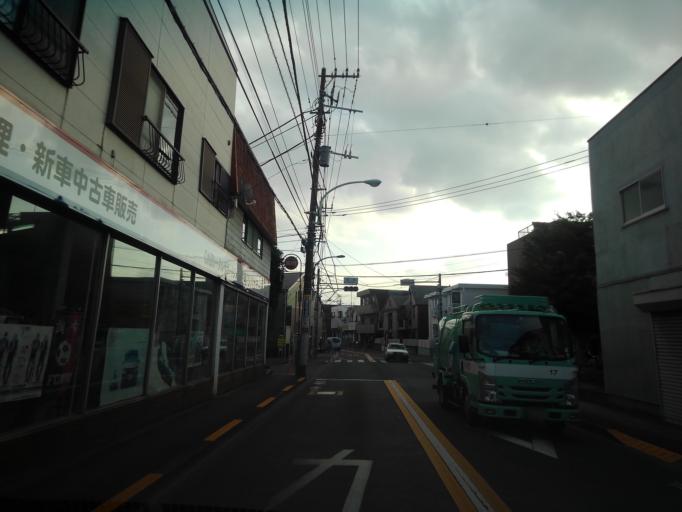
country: JP
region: Tokyo
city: Chofugaoka
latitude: 35.6590
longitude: 139.5519
